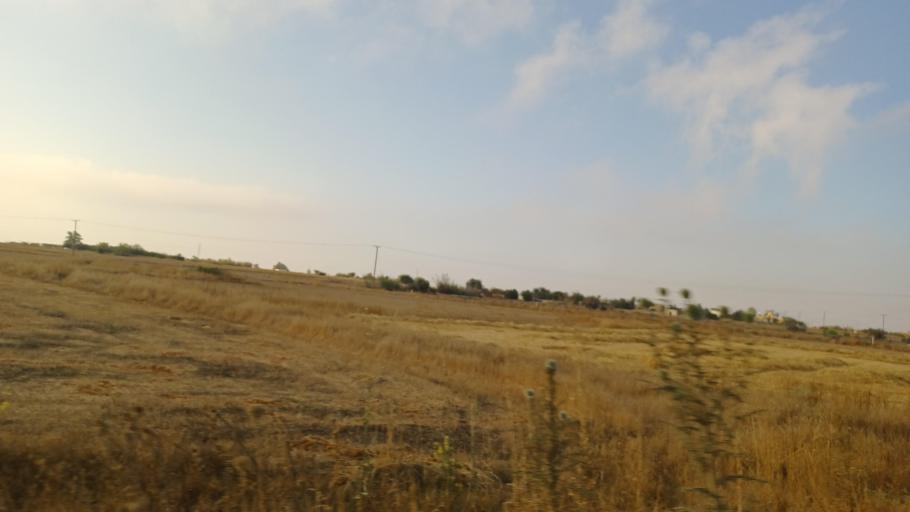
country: CY
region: Ammochostos
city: Avgorou
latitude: 35.0412
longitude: 33.8504
